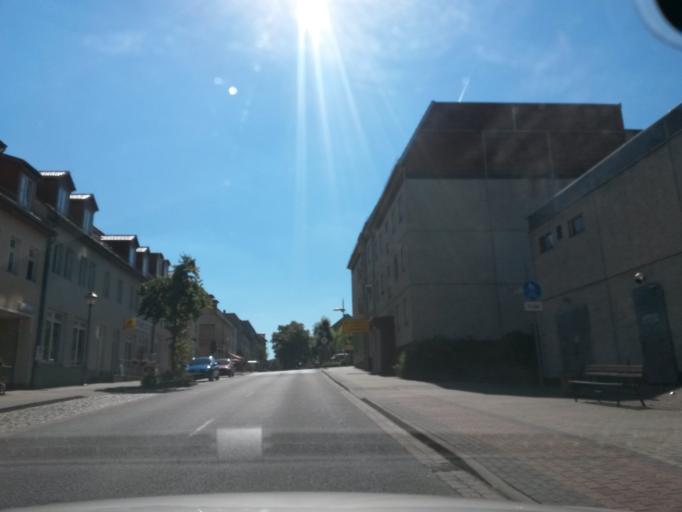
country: DE
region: Brandenburg
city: Lychen
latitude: 53.2111
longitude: 13.3155
